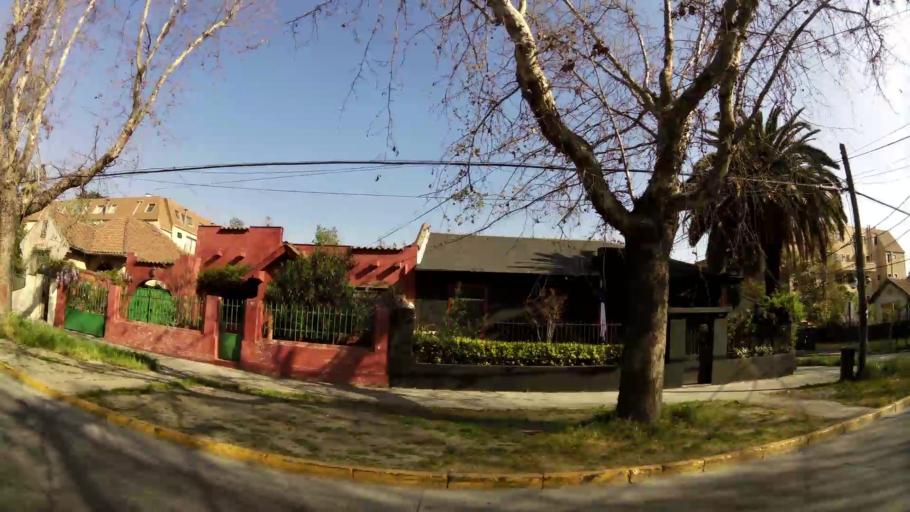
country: CL
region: Santiago Metropolitan
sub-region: Provincia de Santiago
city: Villa Presidente Frei, Nunoa, Santiago, Chile
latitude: -33.4593
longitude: -70.5947
